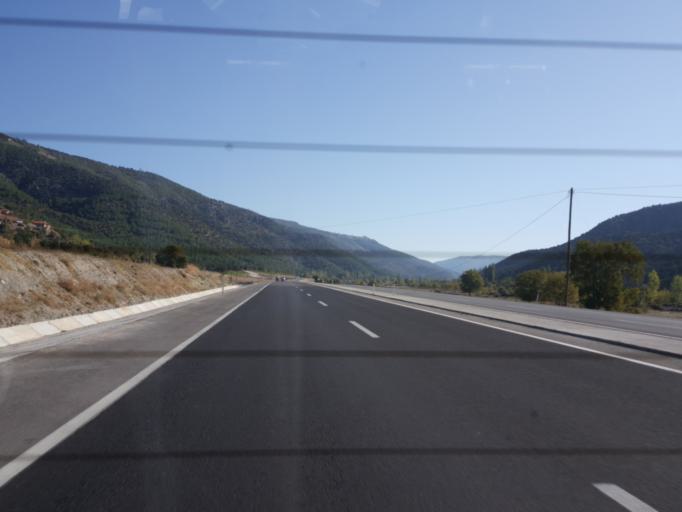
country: TR
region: Tokat
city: Turhal
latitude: 40.4656
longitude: 36.1197
